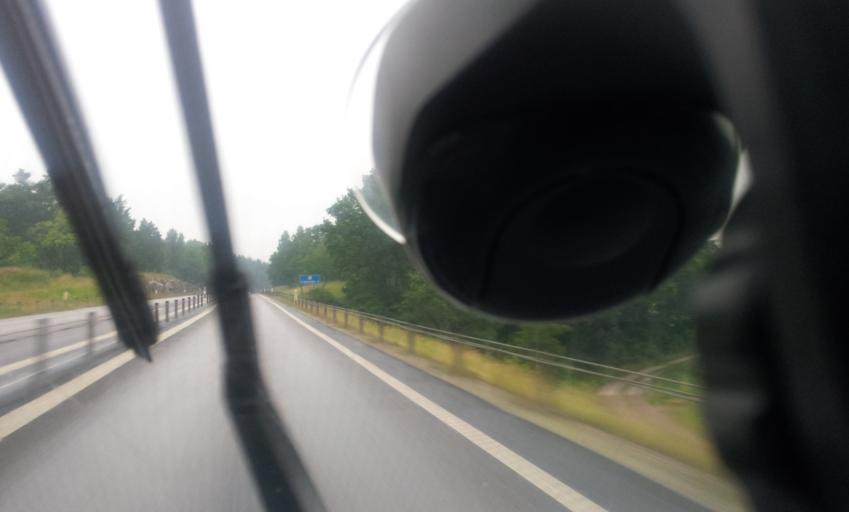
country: SE
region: Kalmar
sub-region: Vasterviks Kommun
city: Gamleby
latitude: 57.9223
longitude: 16.3992
